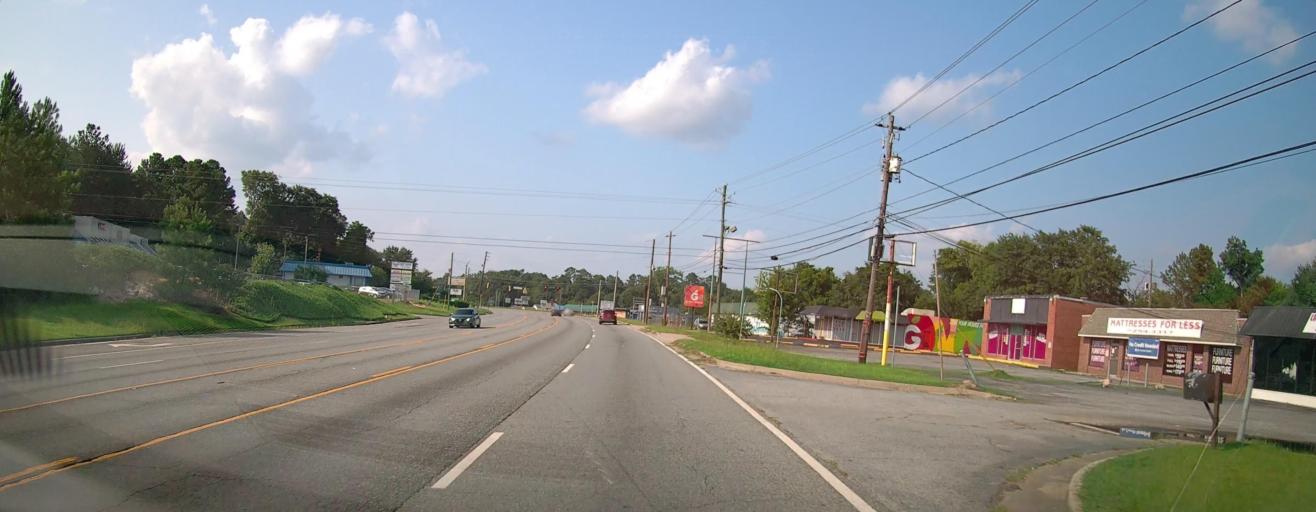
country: US
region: Georgia
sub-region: Bibb County
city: Macon
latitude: 32.8015
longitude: -83.6638
